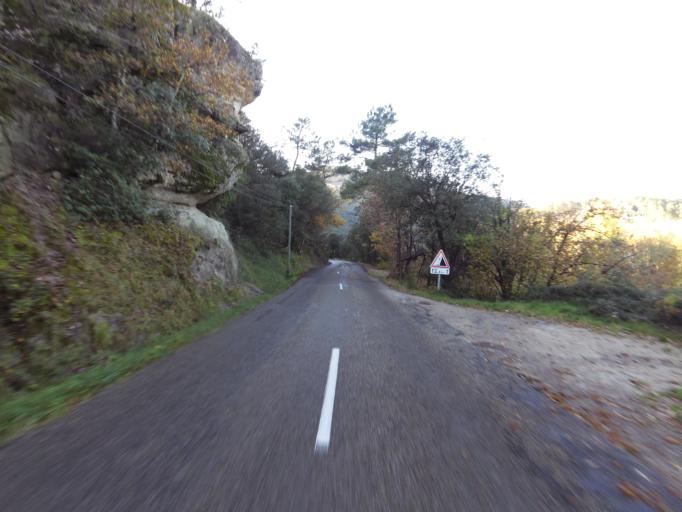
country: FR
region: Rhone-Alpes
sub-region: Departement de l'Ardeche
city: Joyeuse
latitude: 44.4975
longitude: 4.2157
